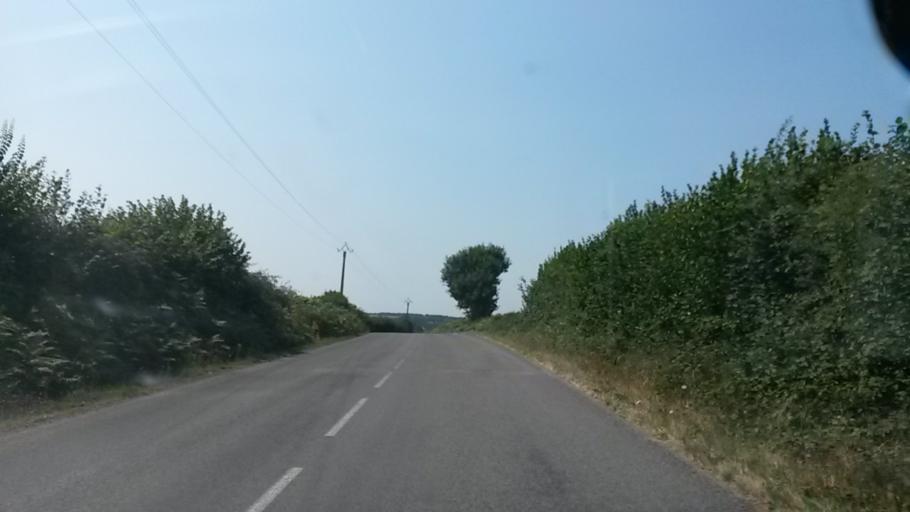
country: FR
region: Pays de la Loire
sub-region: Departement de la Mayenne
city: Saint-Pierre-des-Nids
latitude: 48.3886
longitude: -0.1322
